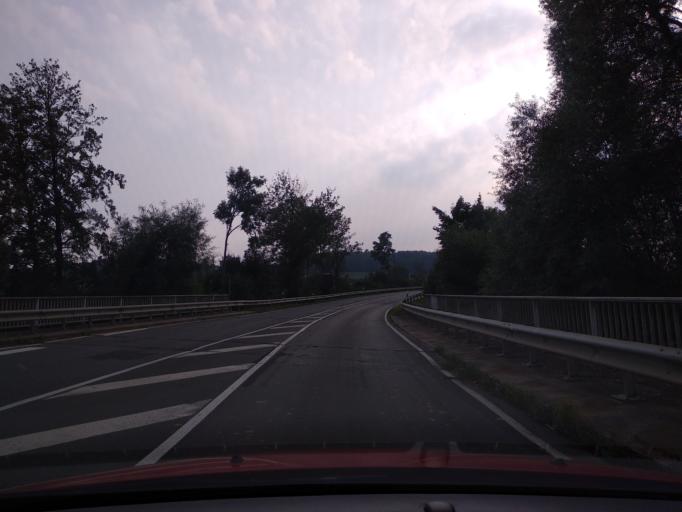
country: DE
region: Hesse
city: Liebenau
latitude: 51.4967
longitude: 9.2950
